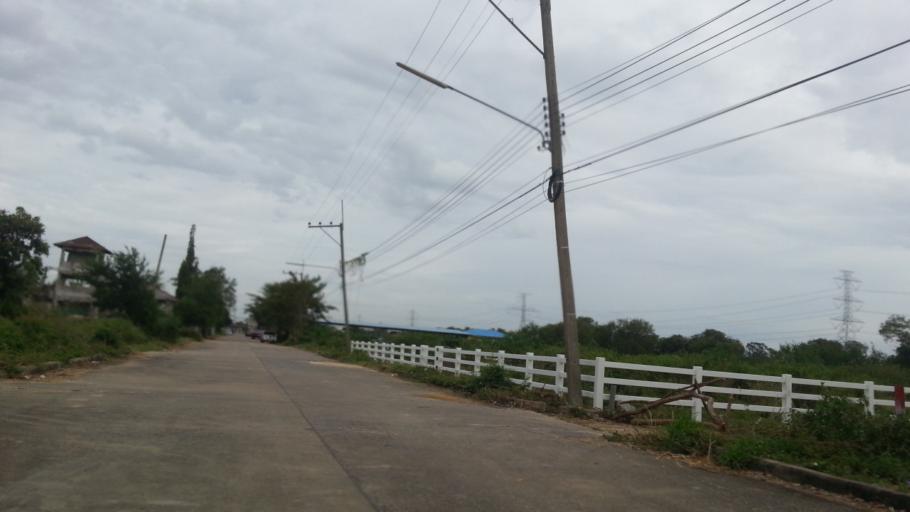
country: TH
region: Pathum Thani
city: Nong Suea
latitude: 14.0667
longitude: 100.8785
